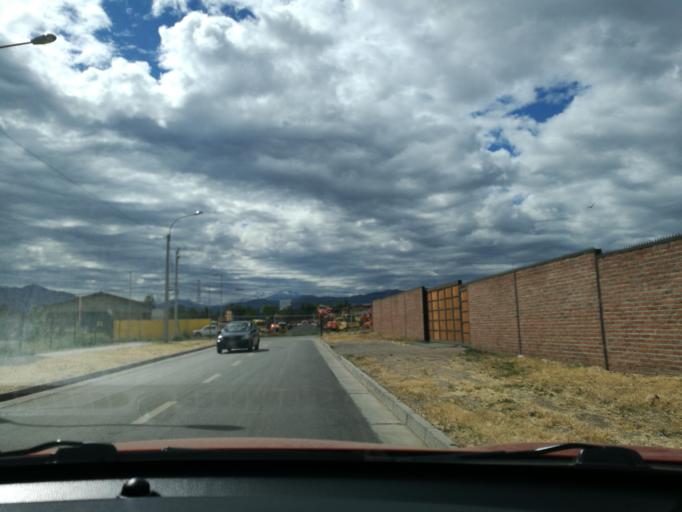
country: CL
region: O'Higgins
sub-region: Provincia de Cachapoal
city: Rancagua
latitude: -34.1615
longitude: -70.7296
